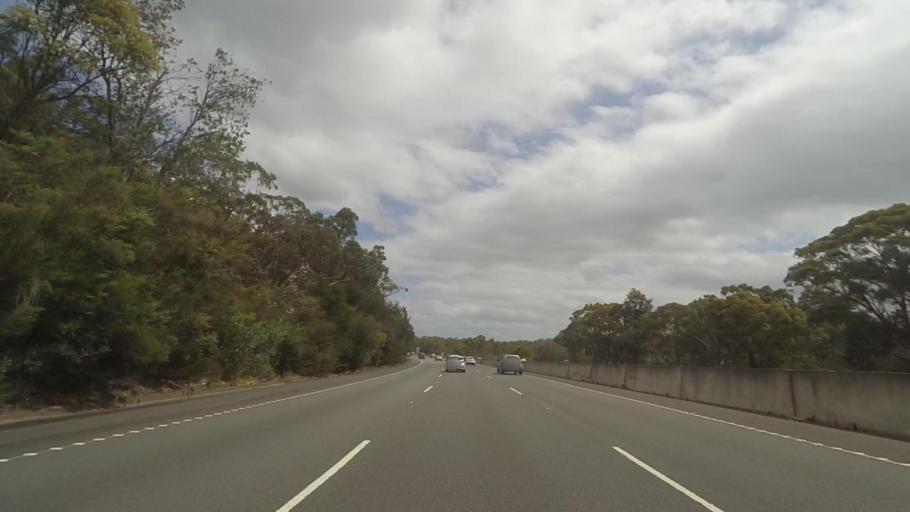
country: AU
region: New South Wales
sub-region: Gosford Shire
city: Point Clare
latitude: -33.4398
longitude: 151.2187
